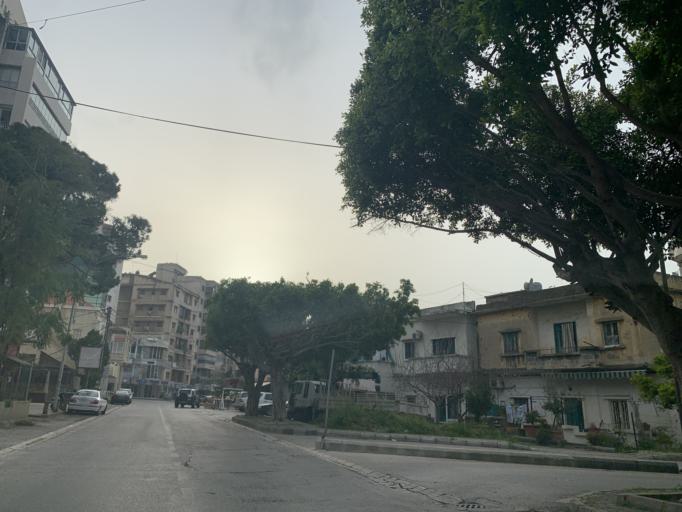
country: LB
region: Mont-Liban
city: Djounie
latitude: 33.9802
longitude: 35.6284
